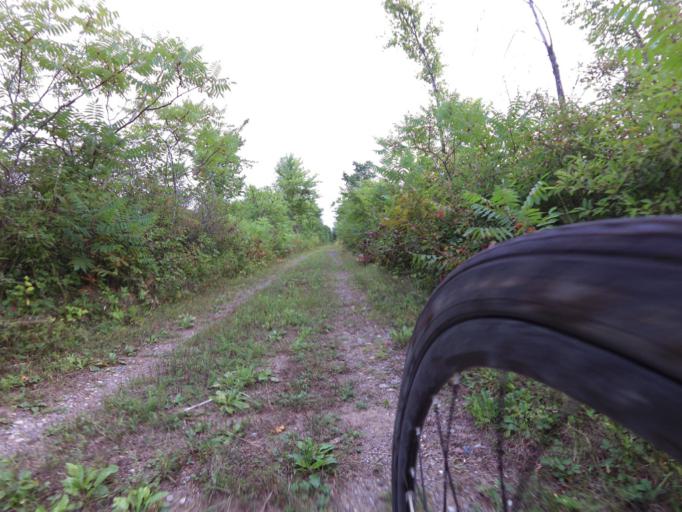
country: CA
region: Ontario
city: Perth
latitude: 44.6301
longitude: -76.2410
